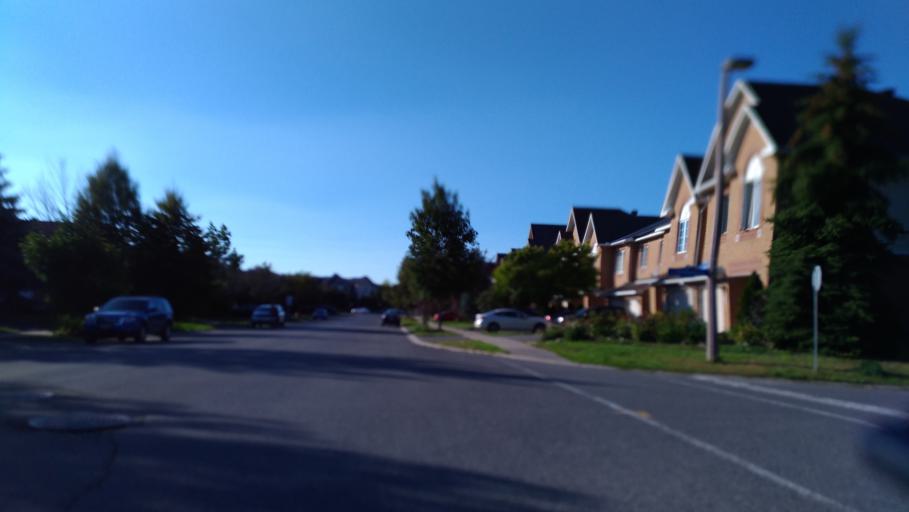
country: CA
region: Ontario
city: Bells Corners
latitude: 45.3489
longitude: -75.9391
